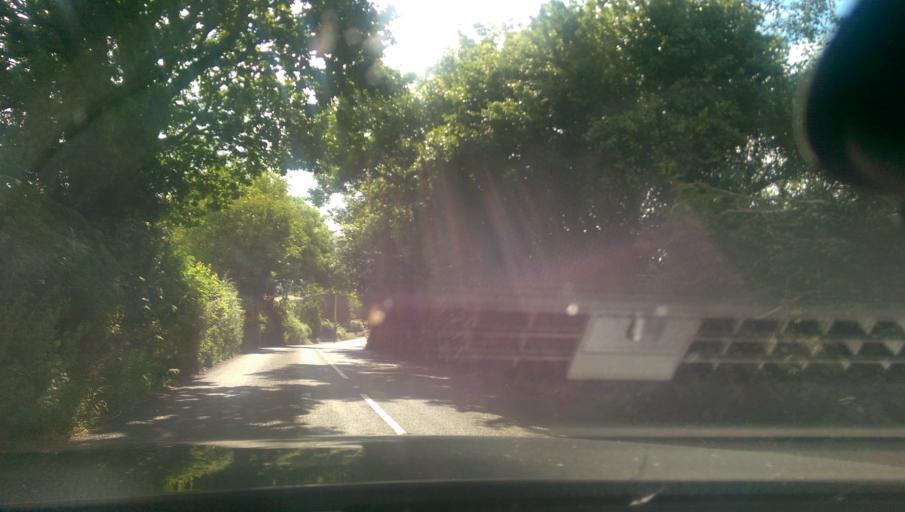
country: GB
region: England
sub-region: Devon
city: Okehampton
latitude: 50.7358
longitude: -3.9377
